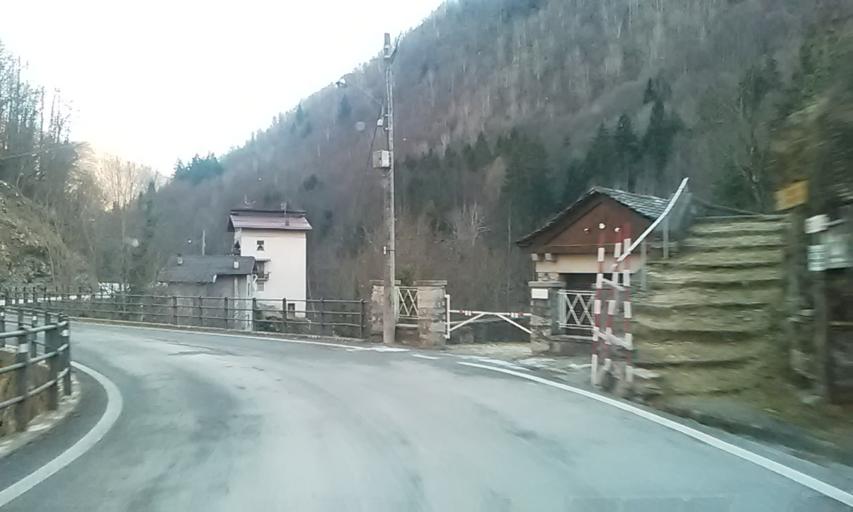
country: IT
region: Piedmont
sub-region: Provincia di Vercelli
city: Boccioleto
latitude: 45.8297
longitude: 8.1151
